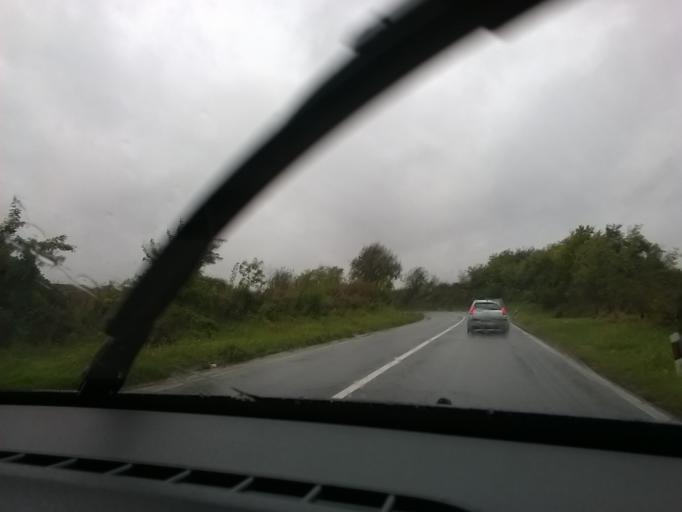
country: RO
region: Caras-Severin
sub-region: Comuna Socol
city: Socol
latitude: 44.9036
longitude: 21.3515
